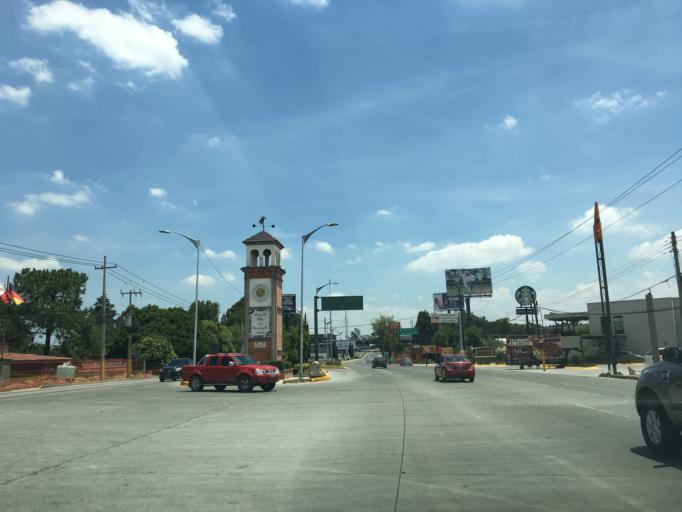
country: MX
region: Puebla
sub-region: Cuautlancingo
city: Sanctorum
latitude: 19.0928
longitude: -98.2296
